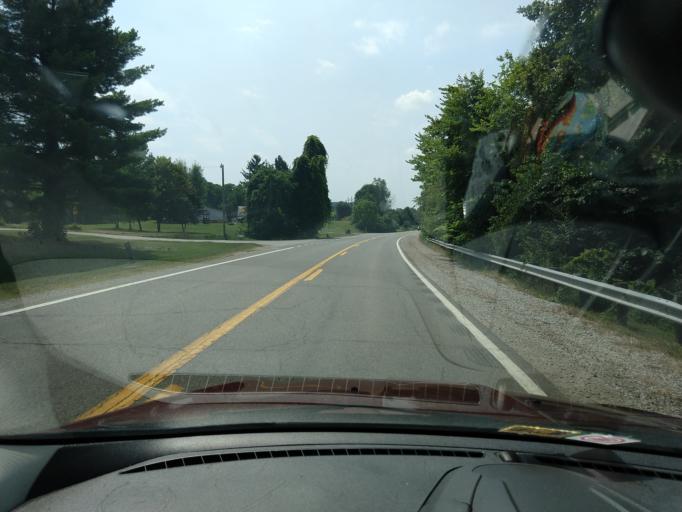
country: US
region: West Virginia
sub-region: Jackson County
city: Ravenswood
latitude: 38.8763
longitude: -81.8272
